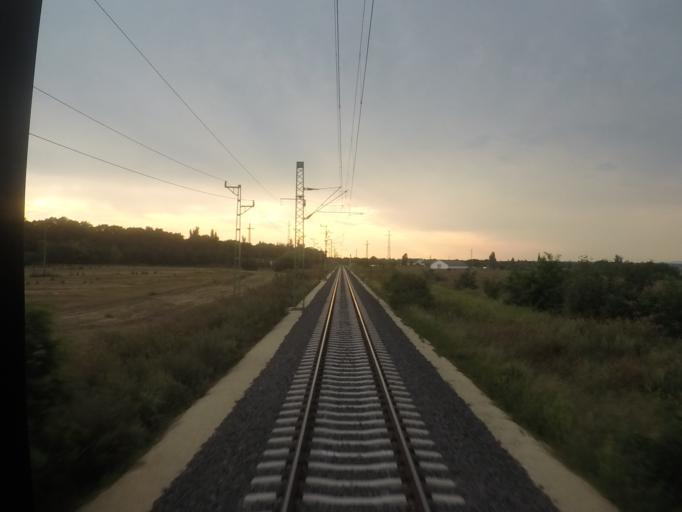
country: HU
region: Fejer
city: Lepseny
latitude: 46.9827
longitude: 18.1980
